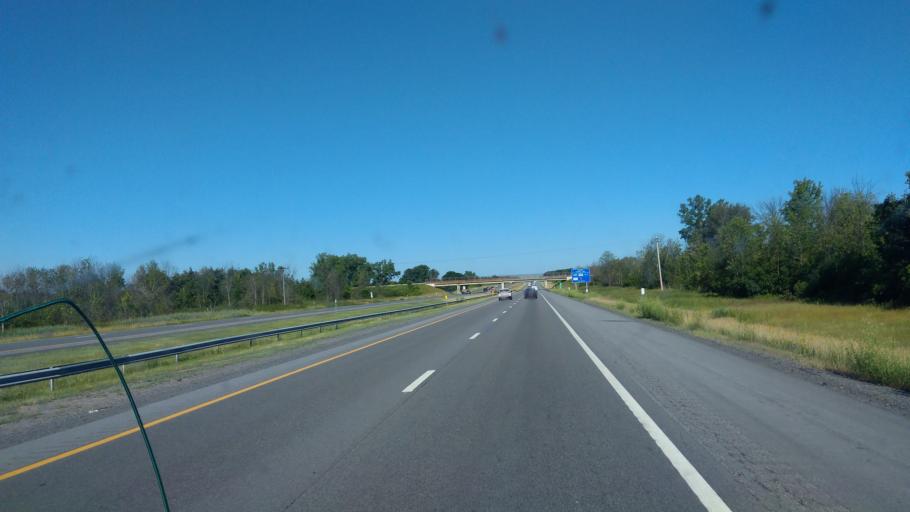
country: US
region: New York
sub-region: Livingston County
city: Caledonia
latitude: 43.0301
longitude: -77.8728
